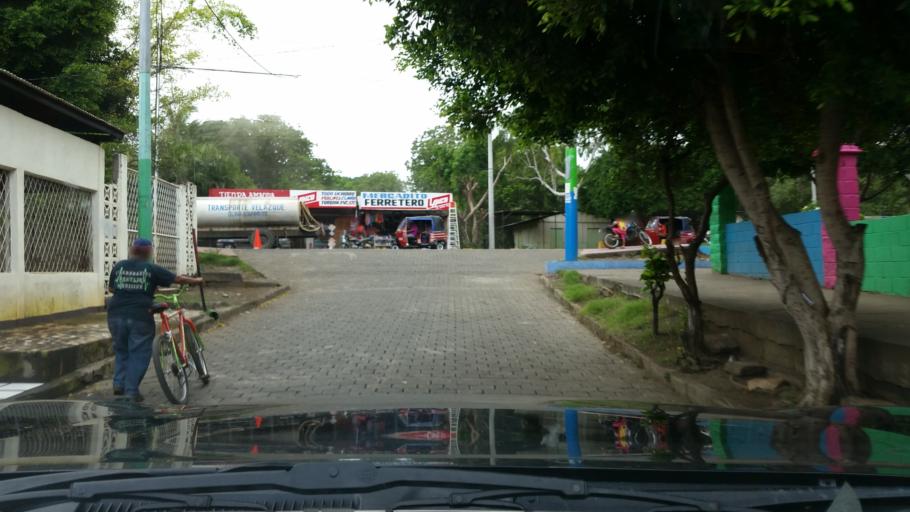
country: NI
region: Masaya
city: Ticuantepe
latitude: 12.0226
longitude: -86.2095
